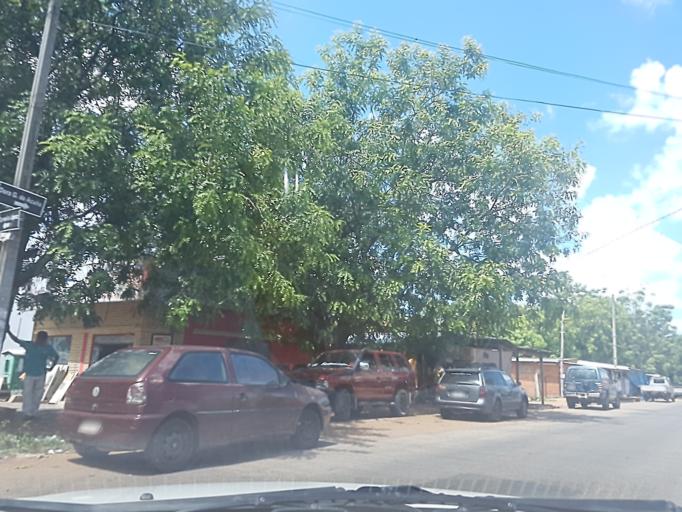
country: PY
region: Central
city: San Lorenzo
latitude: -25.2672
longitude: -57.4832
